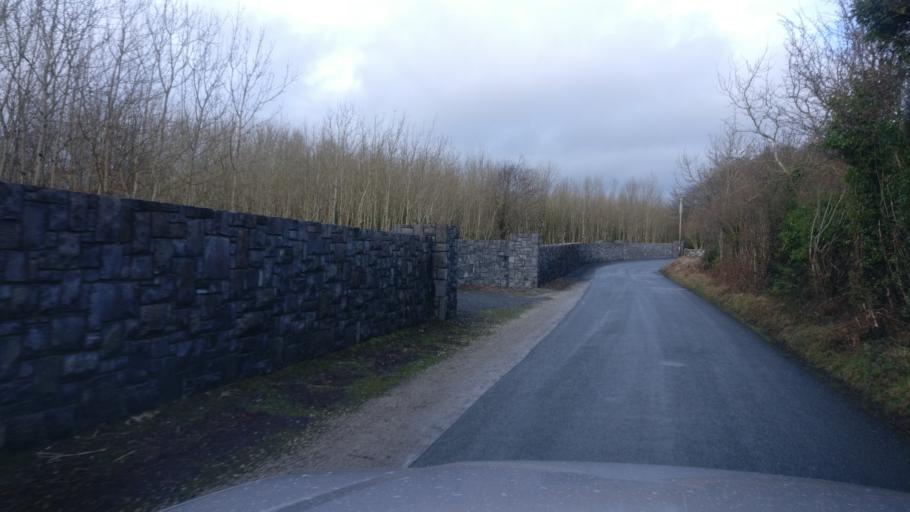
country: IE
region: Connaught
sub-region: County Galway
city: Athenry
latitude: 53.2536
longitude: -8.7233
